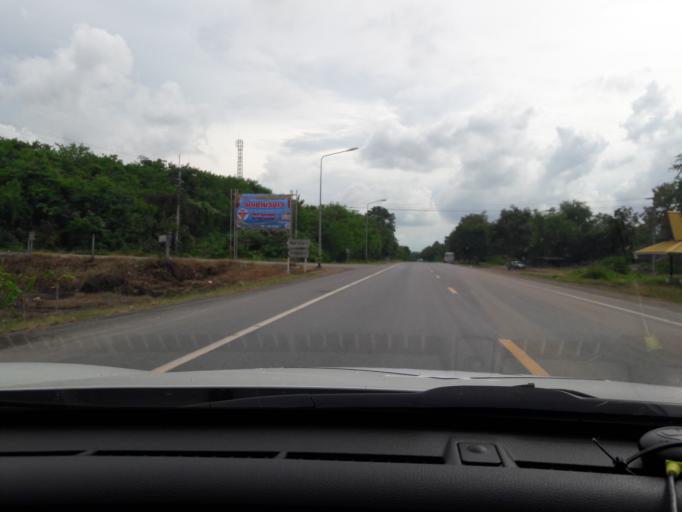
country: TH
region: Nakhon Sawan
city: Tak Fa
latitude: 15.3927
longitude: 100.5092
